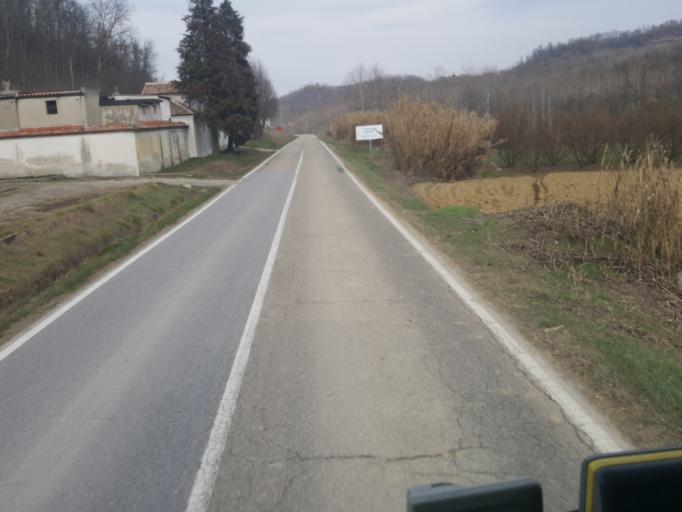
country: IT
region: Piedmont
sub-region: Provincia di Asti
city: Castelnuovo Belbo
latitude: 44.7854
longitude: 8.4163
